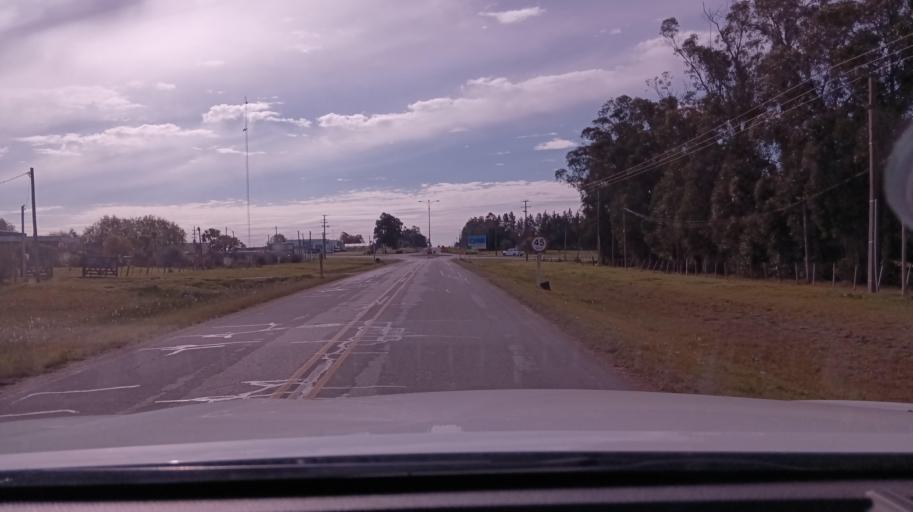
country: UY
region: Canelones
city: Sauce
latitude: -34.6255
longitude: -56.1117
